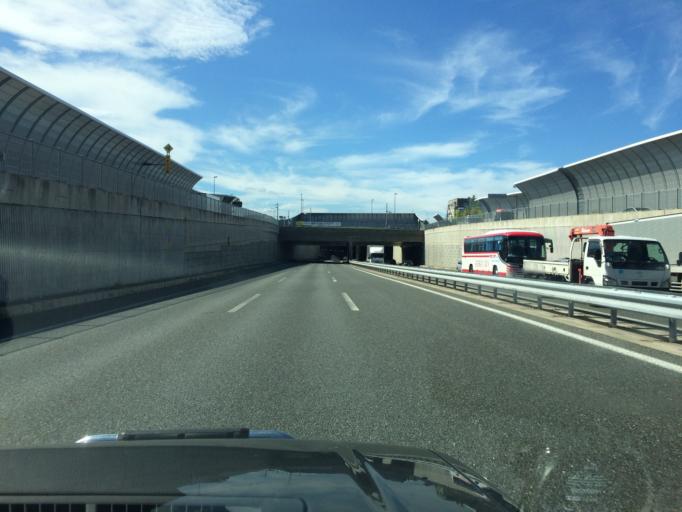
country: JP
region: Osaka
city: Neyagawa
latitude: 34.7606
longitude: 135.6487
